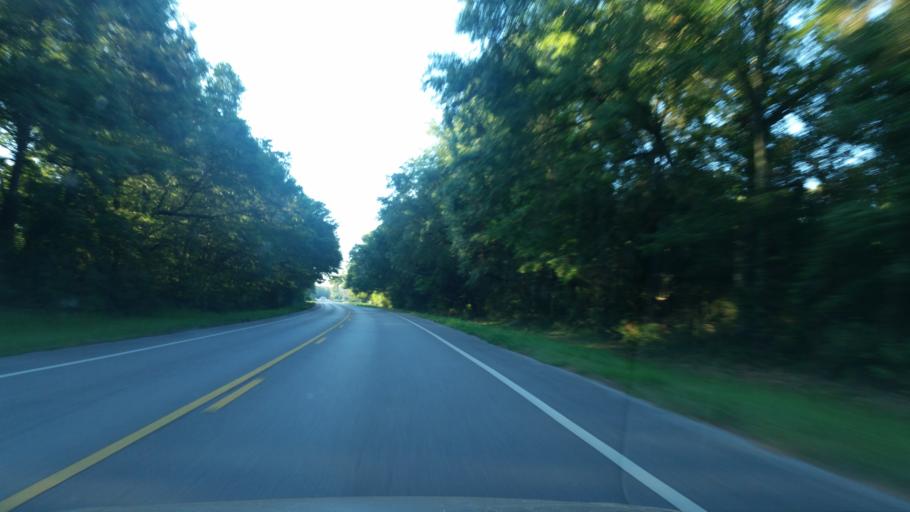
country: US
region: Florida
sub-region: Escambia County
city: Cantonment
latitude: 30.5640
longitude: -87.3455
